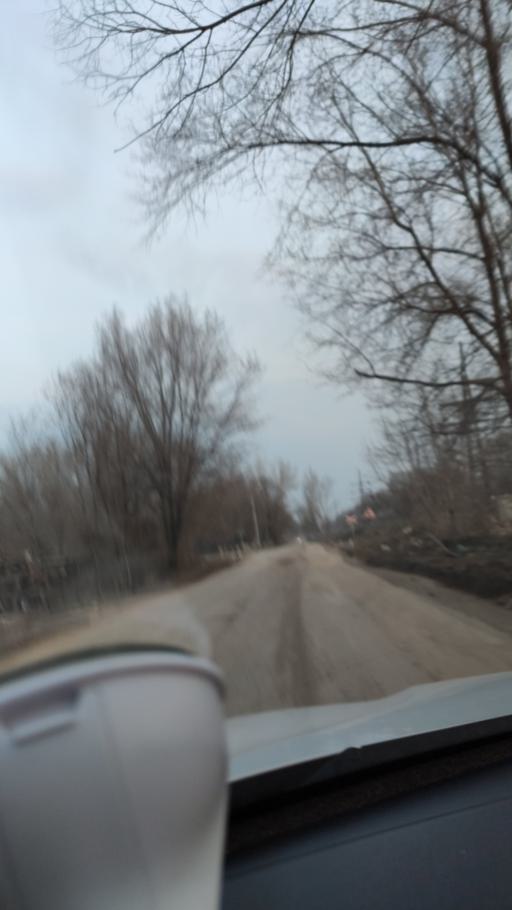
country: RU
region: Samara
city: Samara
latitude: 53.1859
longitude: 50.2593
